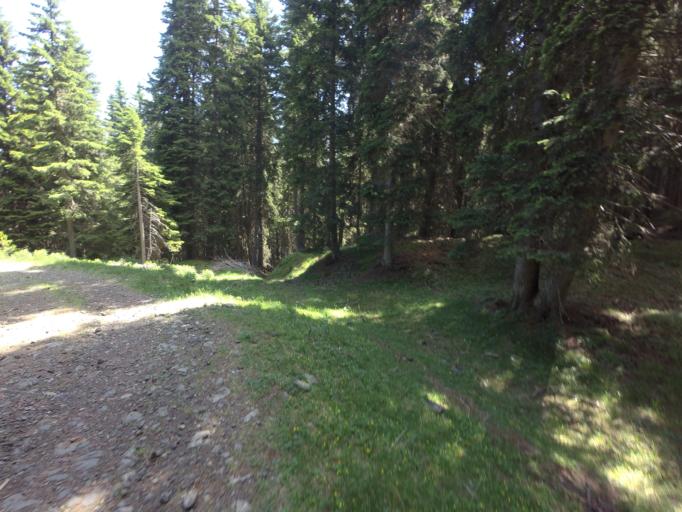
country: IT
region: Trentino-Alto Adige
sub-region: Bolzano
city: Ortisei
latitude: 46.5209
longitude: 11.6568
